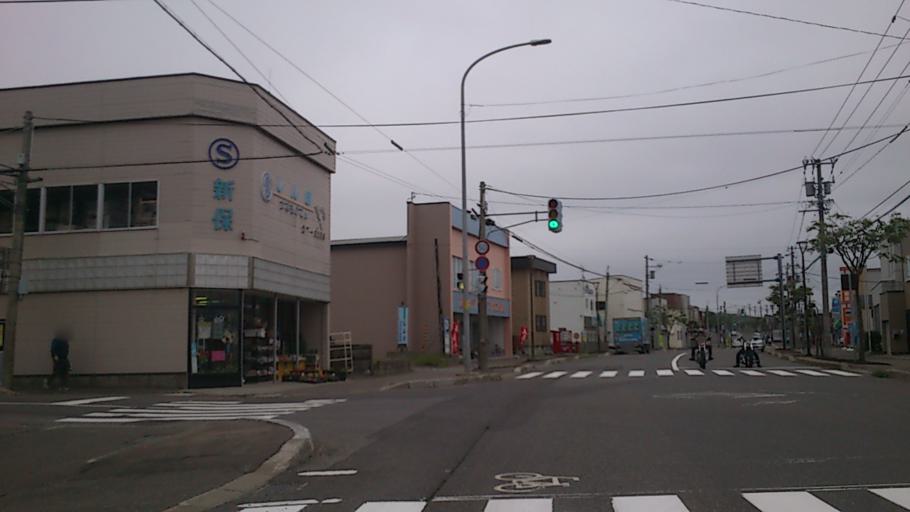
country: JP
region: Hokkaido
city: Iwanai
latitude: 42.4540
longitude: 139.8509
